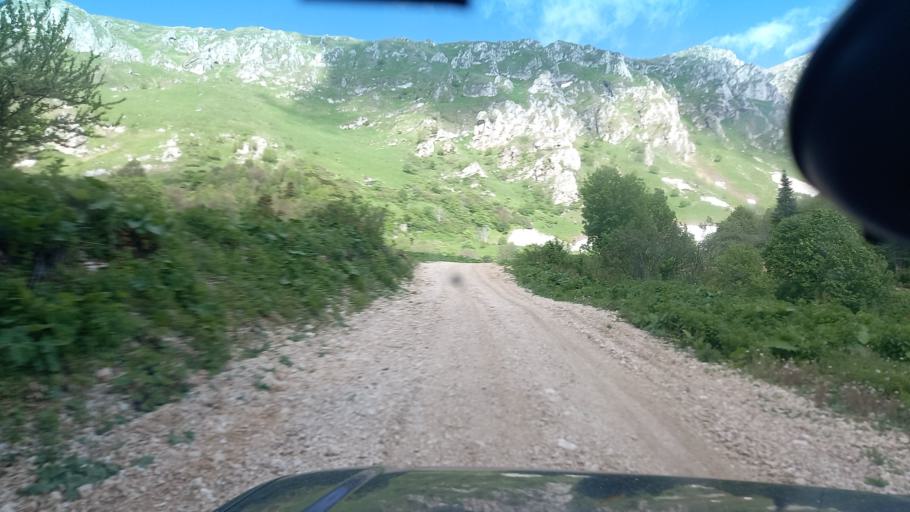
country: RU
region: Krasnodarskiy
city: Neftegorsk
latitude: 44.0116
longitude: 39.8570
